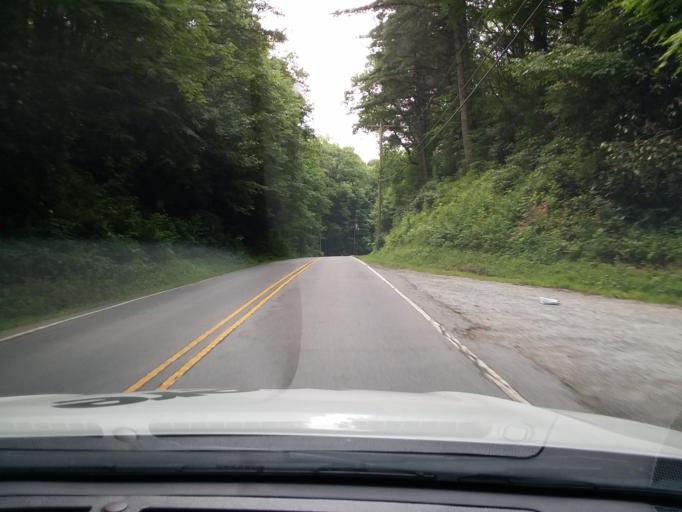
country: US
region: Georgia
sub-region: Rabun County
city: Mountain City
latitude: 35.0475
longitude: -83.2032
